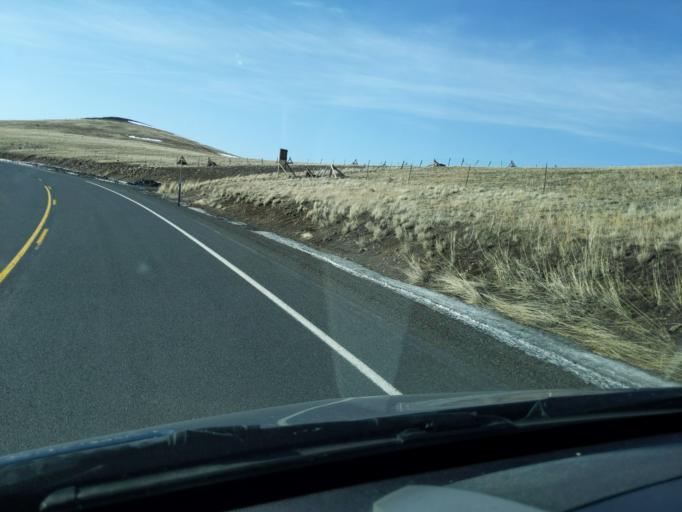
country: US
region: Oregon
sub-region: Umatilla County
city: Pilot Rock
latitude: 45.2996
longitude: -118.9875
